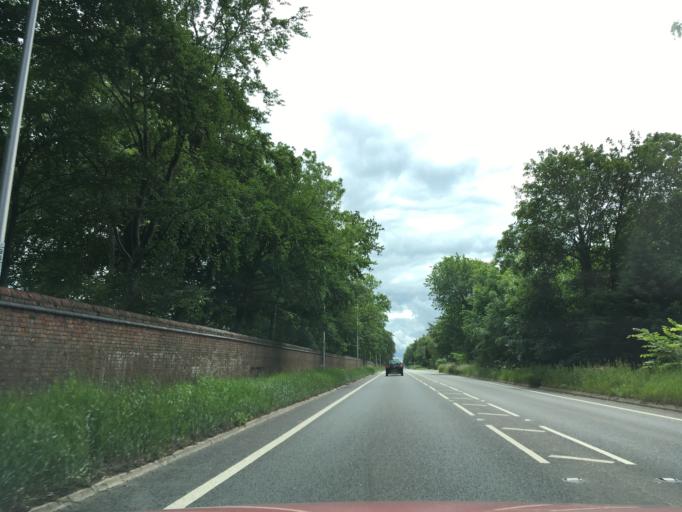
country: GB
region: England
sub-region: Northamptonshire
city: Towcester
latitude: 52.1262
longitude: -0.9798
